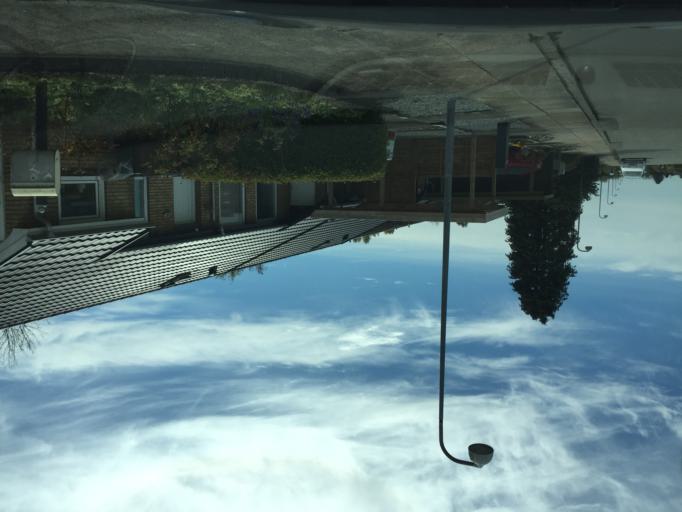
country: DK
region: South Denmark
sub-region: Odense Kommune
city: Odense
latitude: 55.4076
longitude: 10.3261
